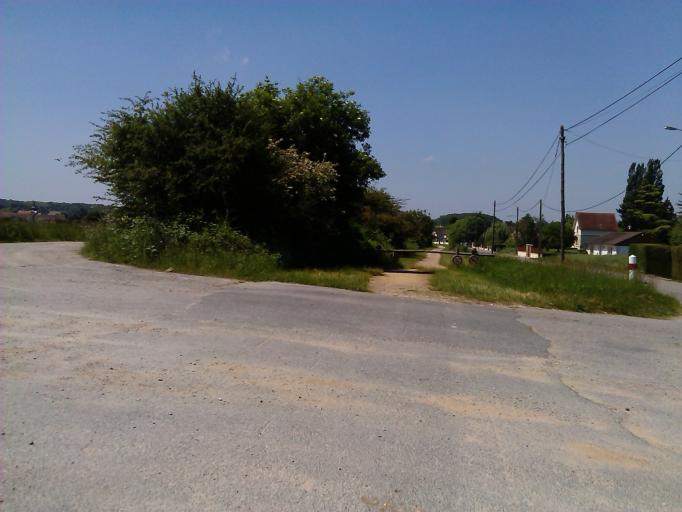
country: FR
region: Centre
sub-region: Departement de l'Indre
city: Saint-Gaultier
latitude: 46.6339
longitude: 1.4393
